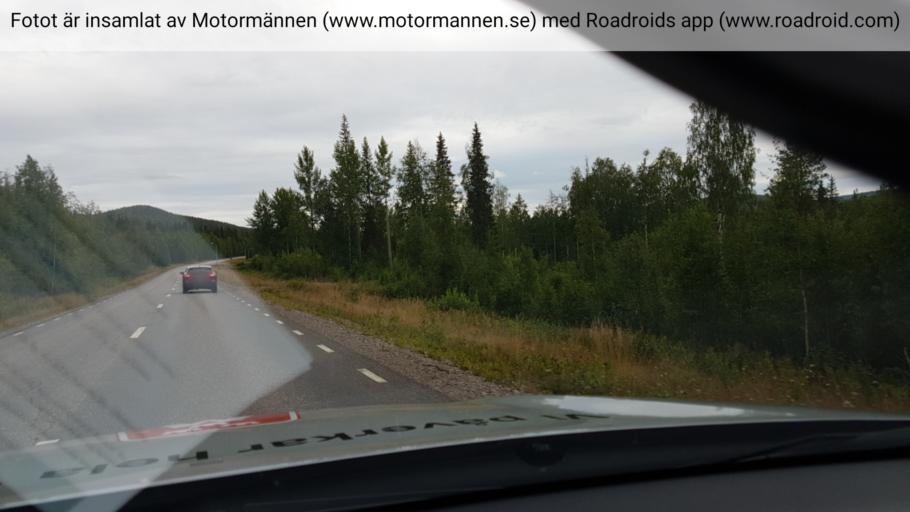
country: SE
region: Norrbotten
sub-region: Overkalix Kommun
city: OEverkalix
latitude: 66.5704
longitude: 22.7598
